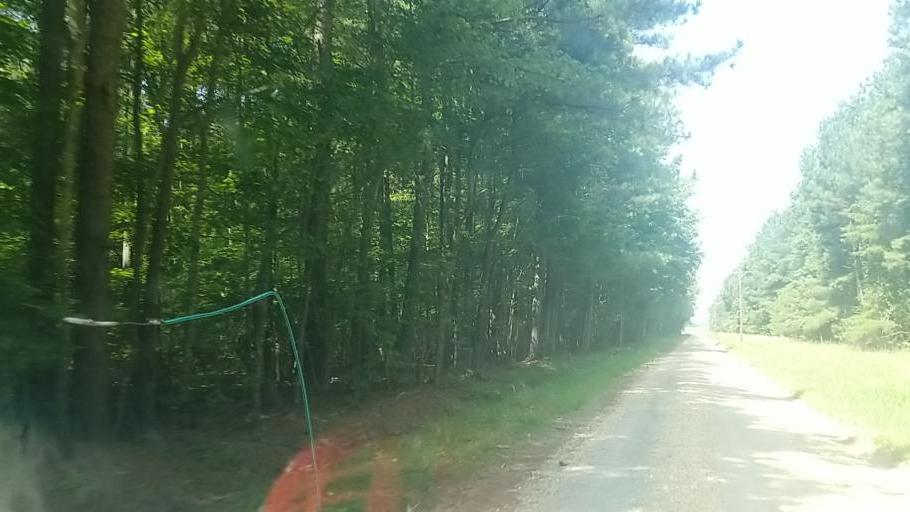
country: US
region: Maryland
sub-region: Caroline County
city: Denton
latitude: 38.8702
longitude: -75.7428
